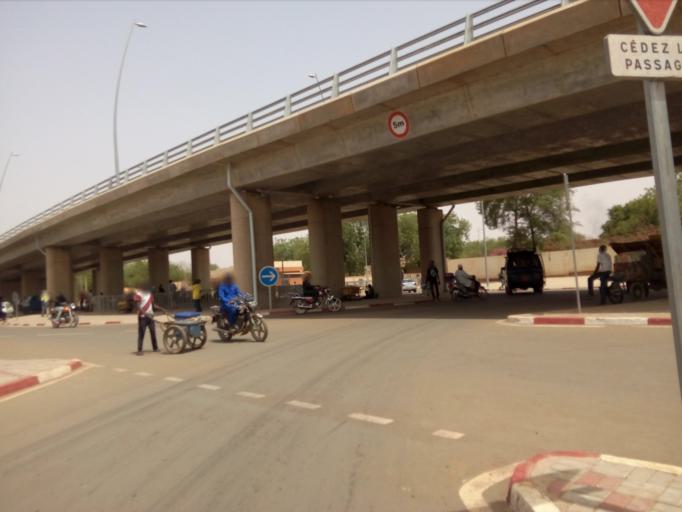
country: NE
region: Niamey
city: Niamey
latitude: 13.5207
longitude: 2.1195
